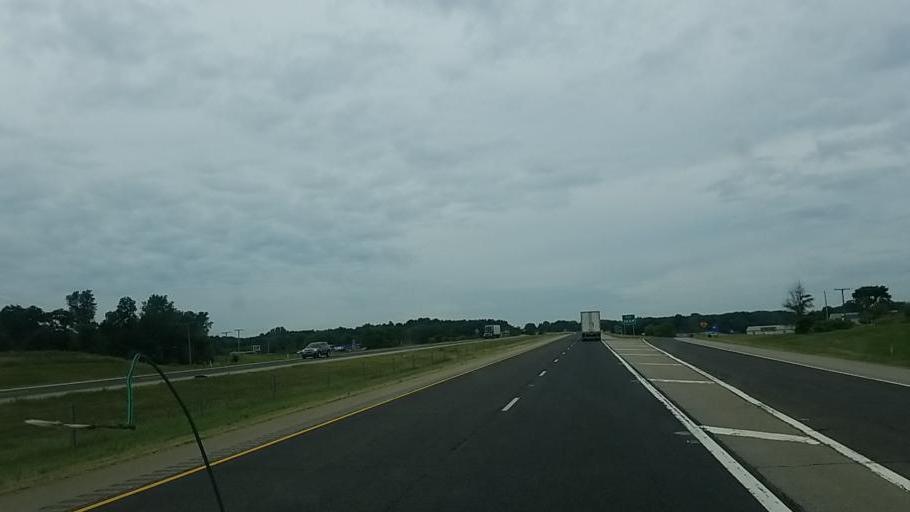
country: US
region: Indiana
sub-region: Steuben County
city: Angola
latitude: 41.6657
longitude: -85.0245
